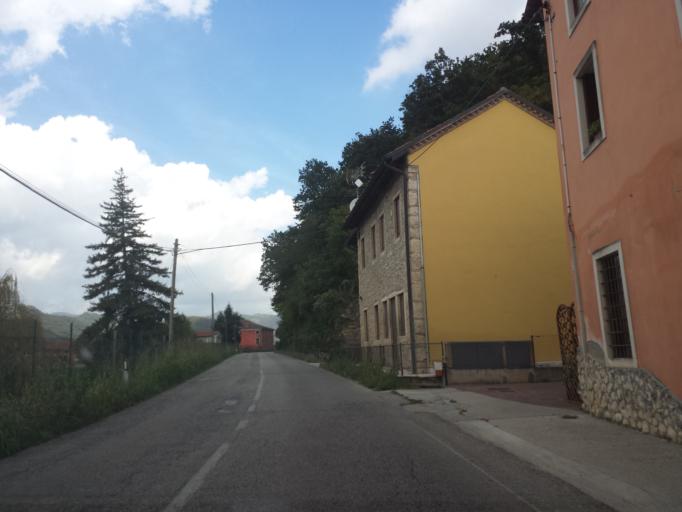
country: IT
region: Veneto
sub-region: Provincia di Vicenza
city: Gambugliano
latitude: 45.5645
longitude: 11.4242
